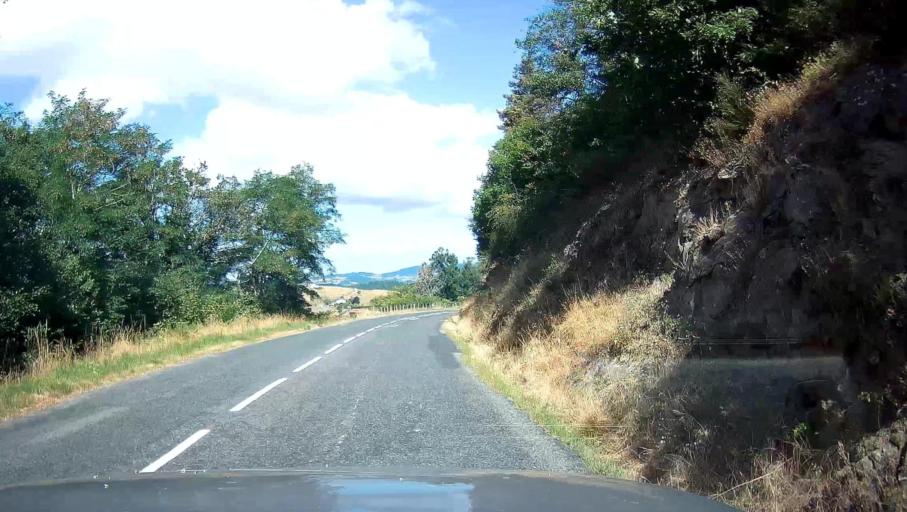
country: FR
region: Rhone-Alpes
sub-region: Departement du Rhone
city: Grandris
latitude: 46.0019
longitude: 4.5430
